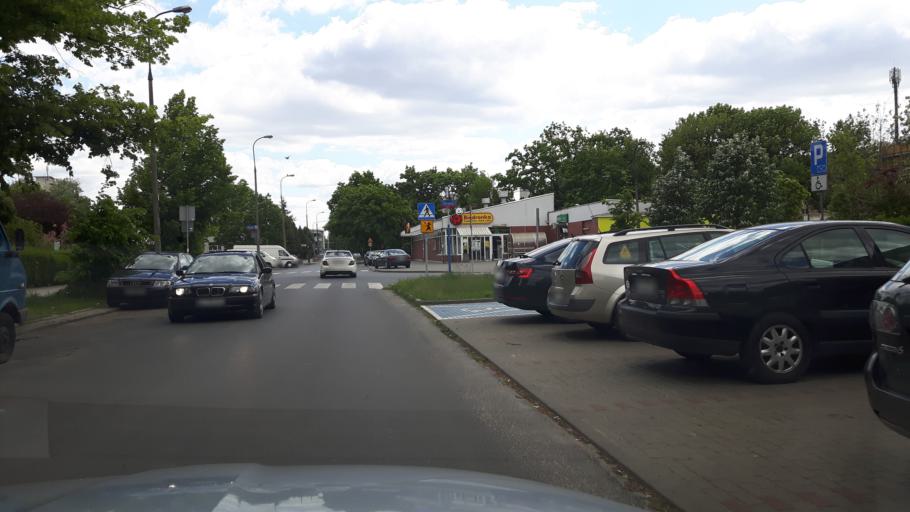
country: PL
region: Masovian Voivodeship
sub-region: Warszawa
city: Targowek
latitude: 52.2951
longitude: 21.0219
